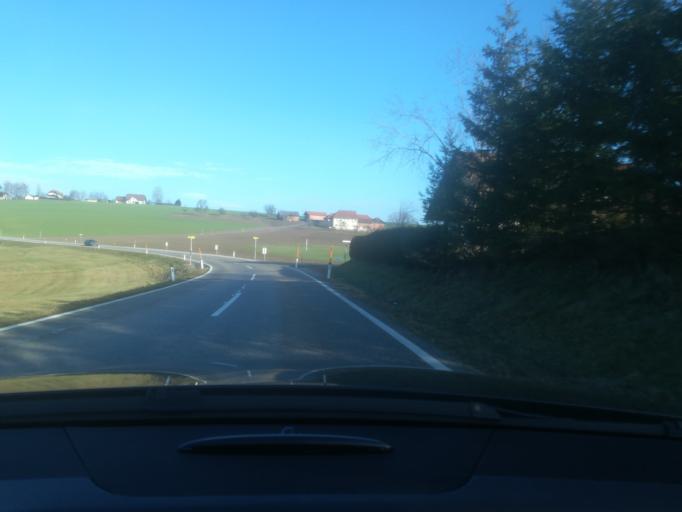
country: AT
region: Upper Austria
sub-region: Politischer Bezirk Urfahr-Umgebung
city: Herzogsdorf
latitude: 48.4001
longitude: 14.0883
